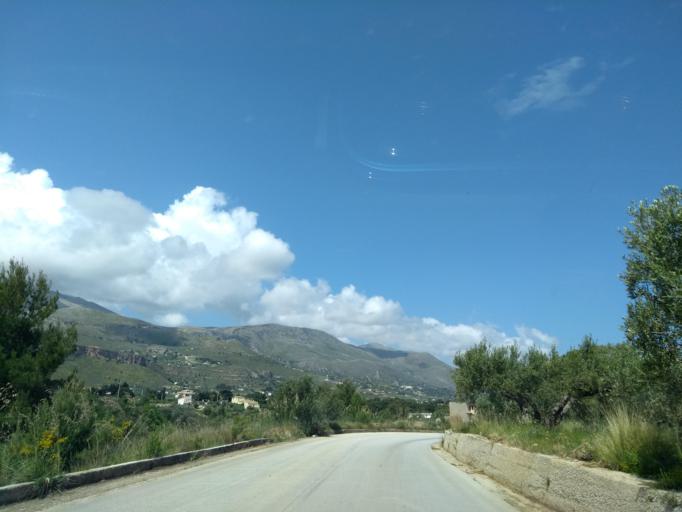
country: IT
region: Sicily
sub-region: Trapani
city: Castellammare del Golfo
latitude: 38.0487
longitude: 12.8418
